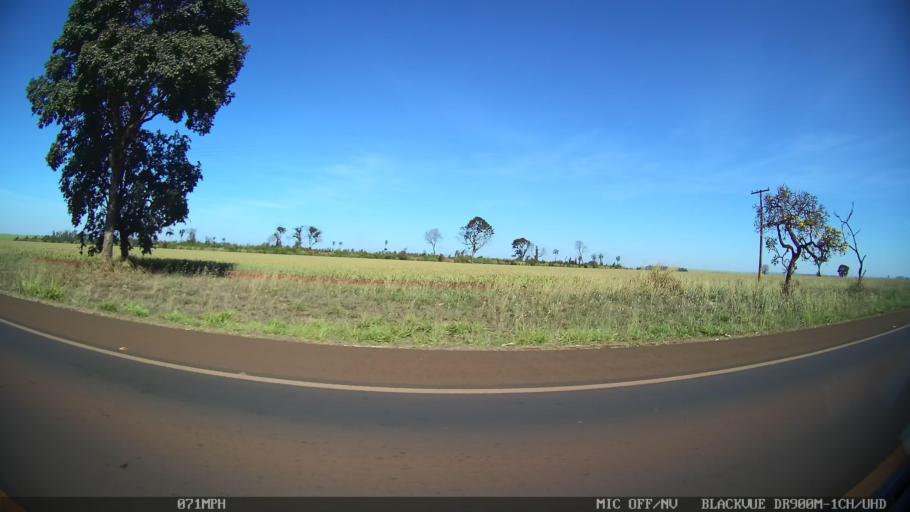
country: BR
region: Sao Paulo
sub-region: Guaira
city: Guaira
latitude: -20.4453
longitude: -48.3958
